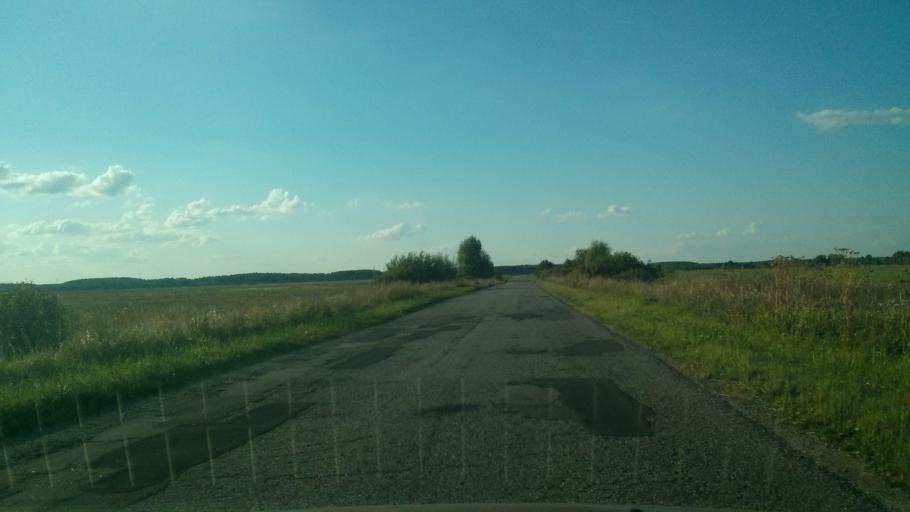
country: RU
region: Vladimir
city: Melenki
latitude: 55.3055
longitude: 41.7876
